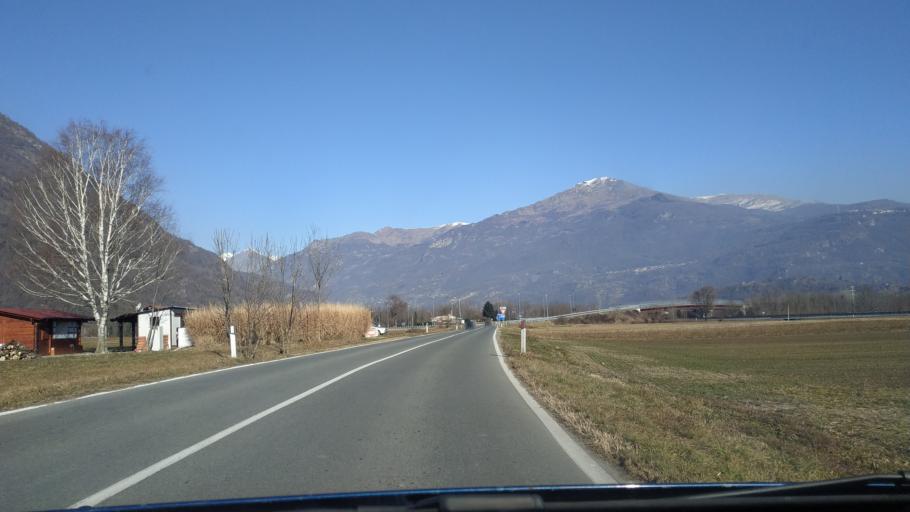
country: IT
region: Piedmont
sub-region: Provincia di Torino
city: Lessolo
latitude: 45.4974
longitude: 7.8285
